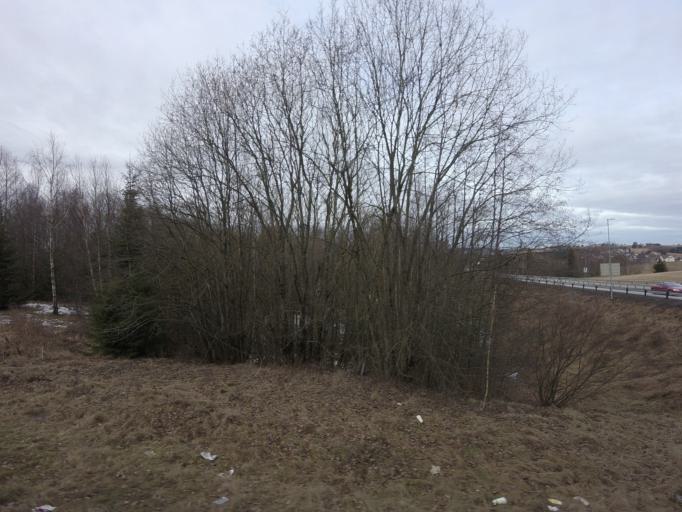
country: NO
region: Akershus
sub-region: Fet
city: Fetsund
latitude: 59.9220
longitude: 11.1837
